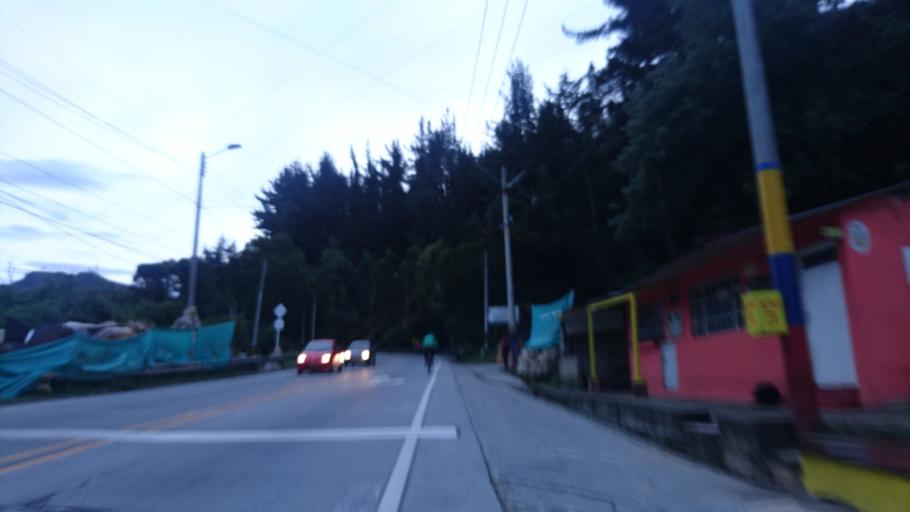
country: CO
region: Bogota D.C.
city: Barrio San Luis
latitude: 4.6753
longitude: -74.0283
